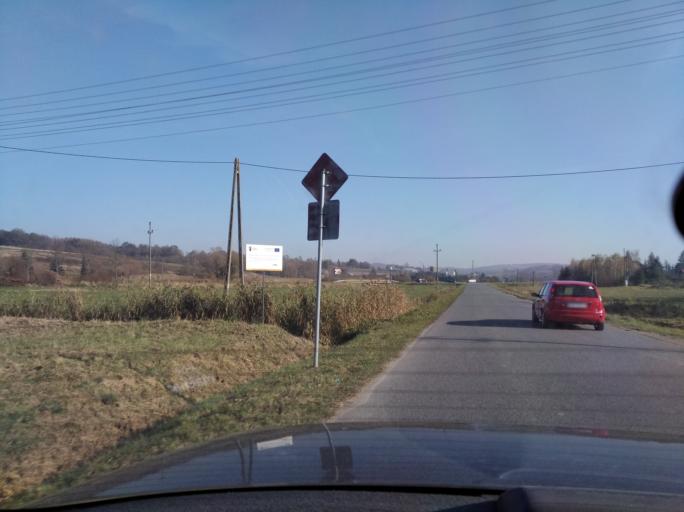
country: PL
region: Subcarpathian Voivodeship
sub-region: Powiat ropczycko-sedziszowski
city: Wielopole Skrzynskie
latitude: 49.9463
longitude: 21.6097
